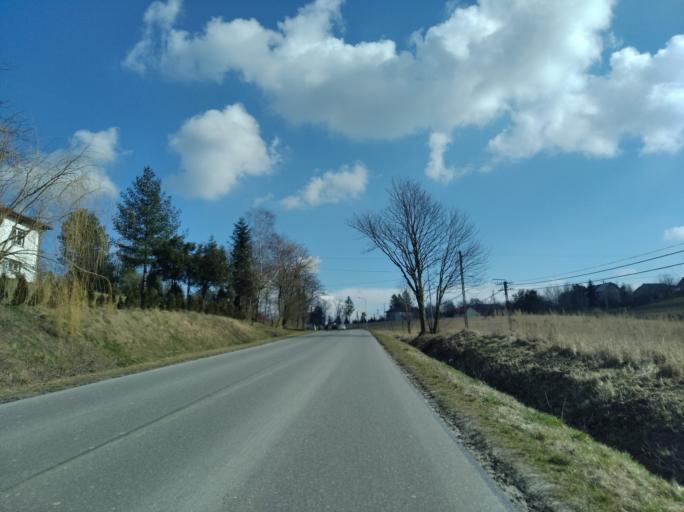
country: PL
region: Subcarpathian Voivodeship
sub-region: Powiat strzyzowski
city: Frysztak
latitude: 49.8491
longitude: 21.5222
